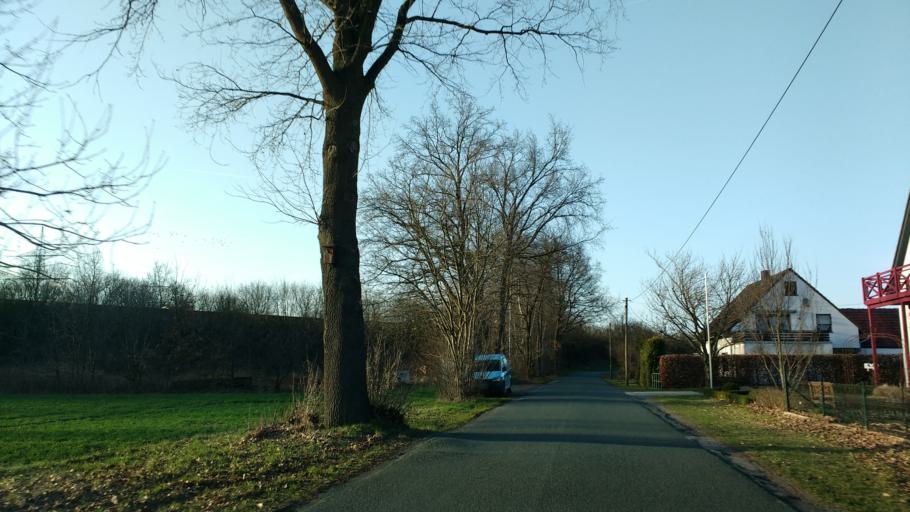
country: DE
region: North Rhine-Westphalia
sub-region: Regierungsbezirk Detmold
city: Hovelhof
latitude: 51.7771
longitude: 8.7035
